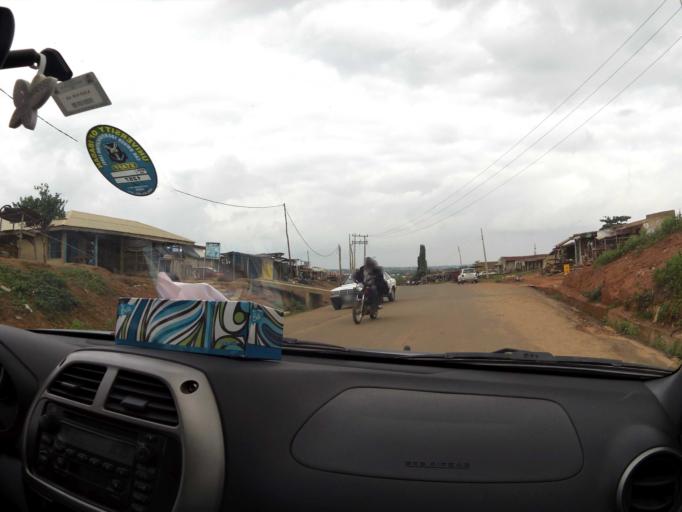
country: NG
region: Oyo
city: Moniya
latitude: 7.5274
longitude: 3.9180
